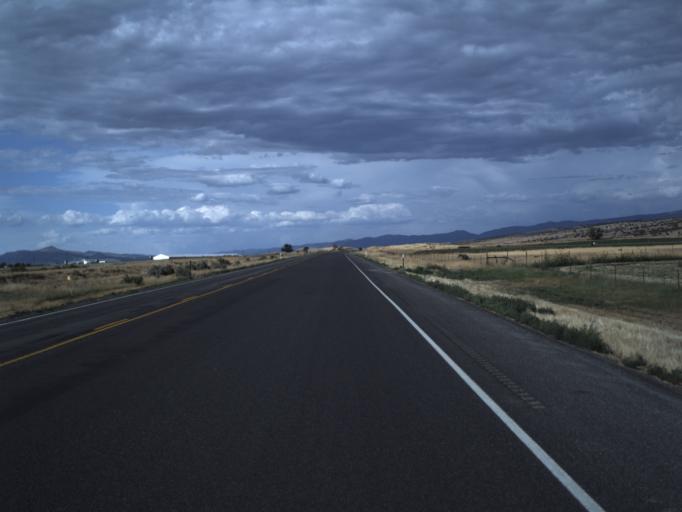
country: US
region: Utah
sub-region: Sanpete County
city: Ephraim
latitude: 39.3873
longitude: -111.5816
